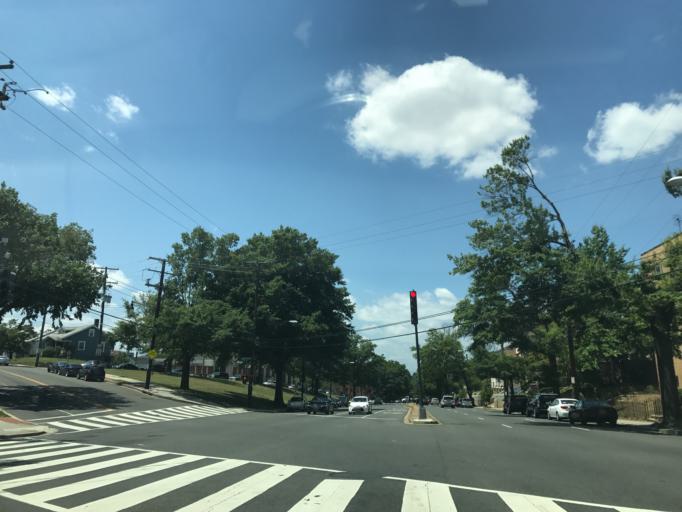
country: US
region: Maryland
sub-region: Prince George's County
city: Mount Rainier
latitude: 38.9239
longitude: -76.9879
